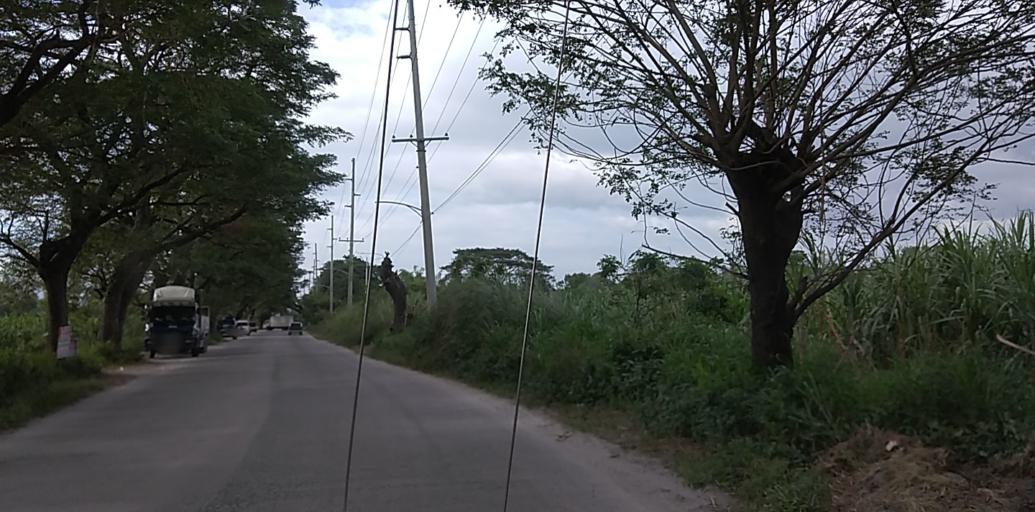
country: PH
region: Central Luzon
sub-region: Province of Pampanga
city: Porac
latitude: 15.0778
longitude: 120.5493
